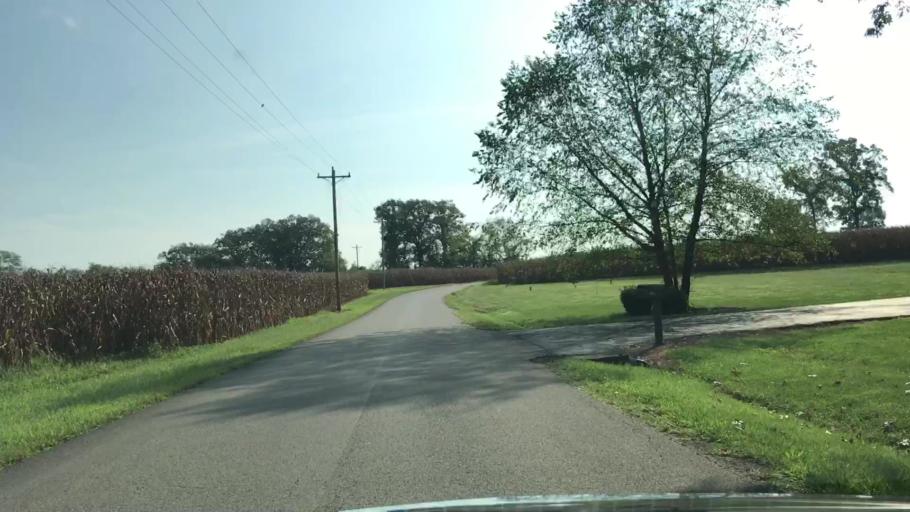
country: US
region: Kentucky
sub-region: Todd County
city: Elkton
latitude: 36.7671
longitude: -87.1601
